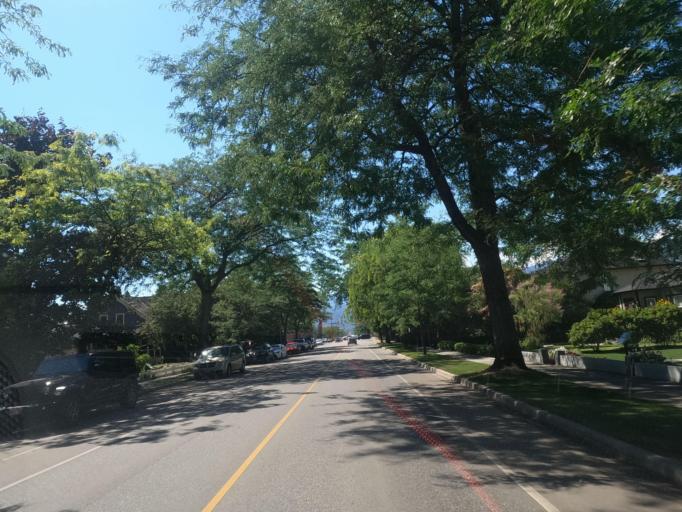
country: CA
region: British Columbia
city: Kelowna
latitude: 49.8864
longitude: -119.4860
